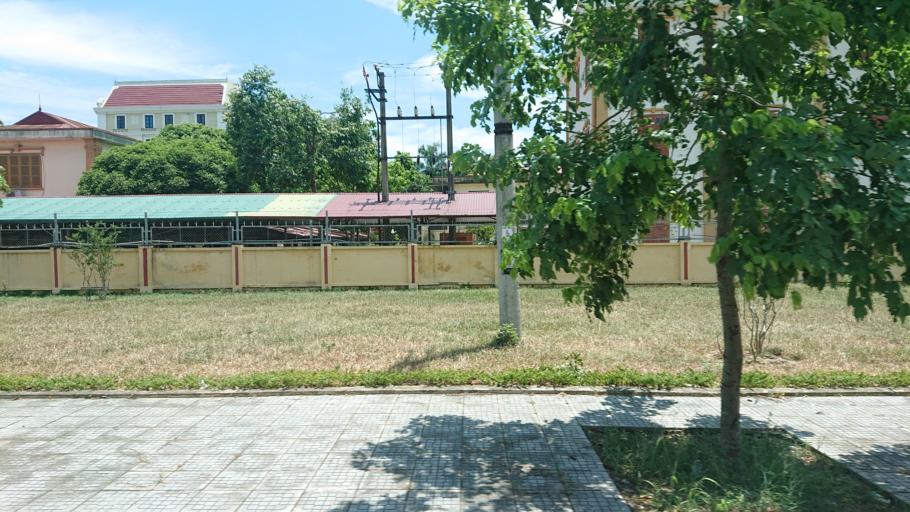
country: VN
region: Ninh Binh
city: Thanh Pho Ninh Binh
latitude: 20.2693
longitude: 105.9718
